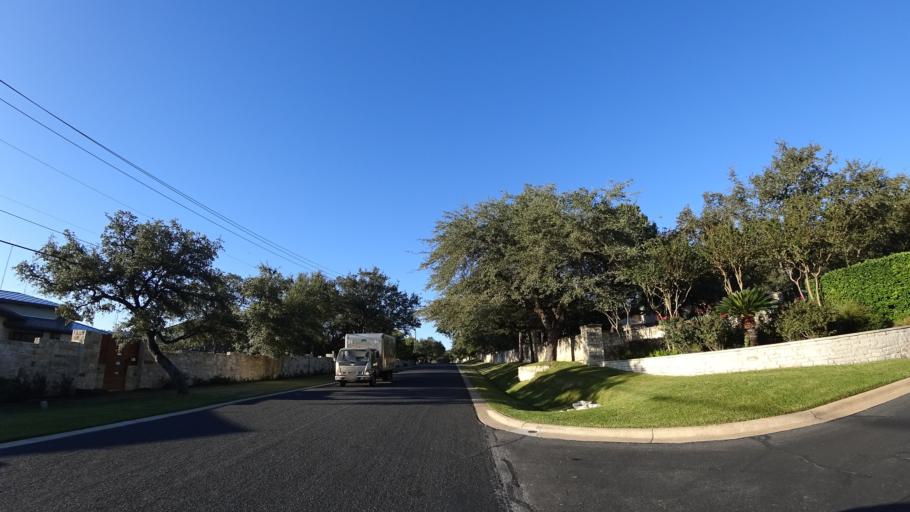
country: US
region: Texas
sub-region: Travis County
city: West Lake Hills
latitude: 30.3398
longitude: -97.8102
